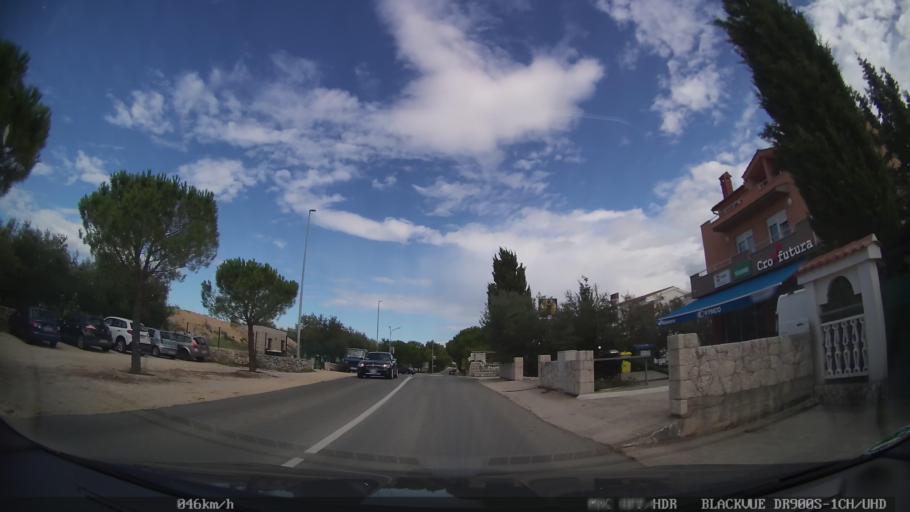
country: HR
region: Primorsko-Goranska
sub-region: Grad Krk
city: Krk
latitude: 45.0316
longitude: 14.5722
